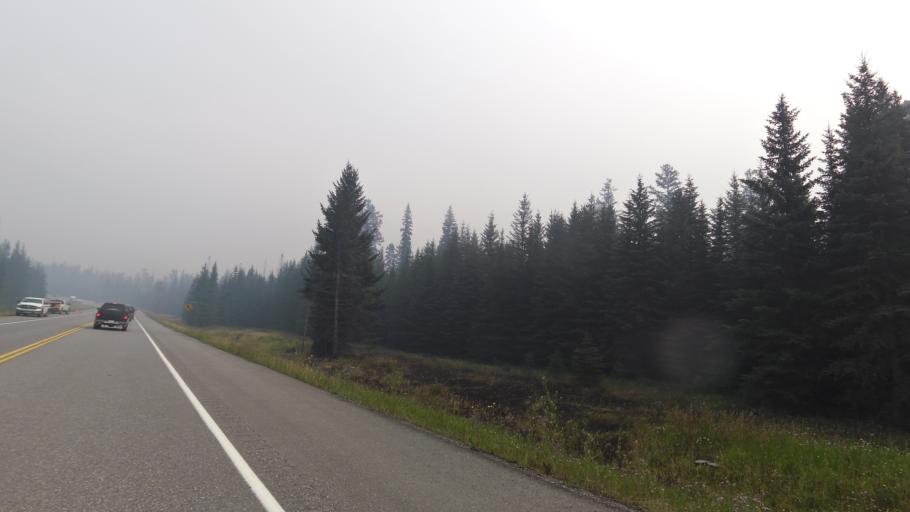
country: CA
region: British Columbia
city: Invermere
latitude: 50.9513
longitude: -115.9647
